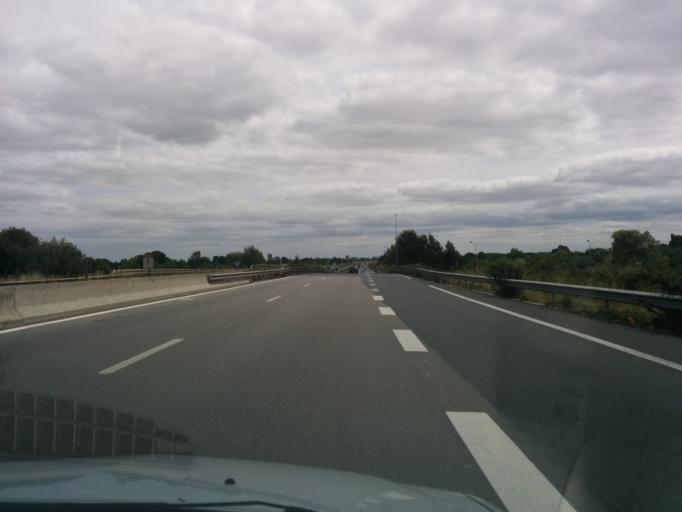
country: FR
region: Pays de la Loire
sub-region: Departement de la Loire-Atlantique
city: Sainte-Luce-sur-Loire
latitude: 47.2371
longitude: -1.4815
